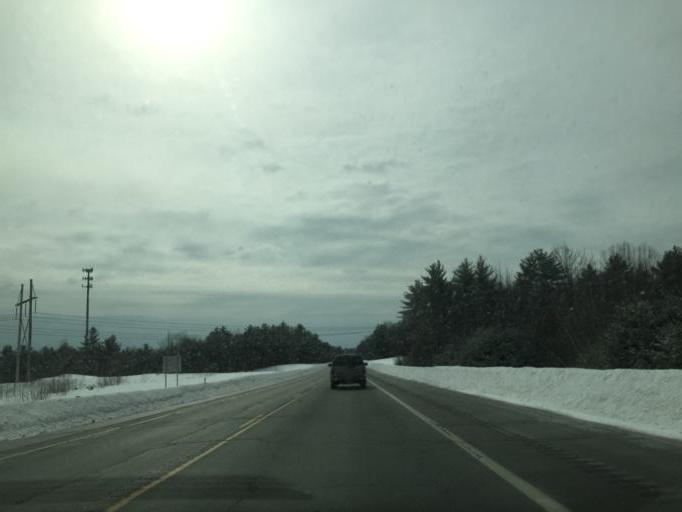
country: US
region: New Hampshire
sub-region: Strafford County
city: Rochester
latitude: 43.3508
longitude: -70.9856
